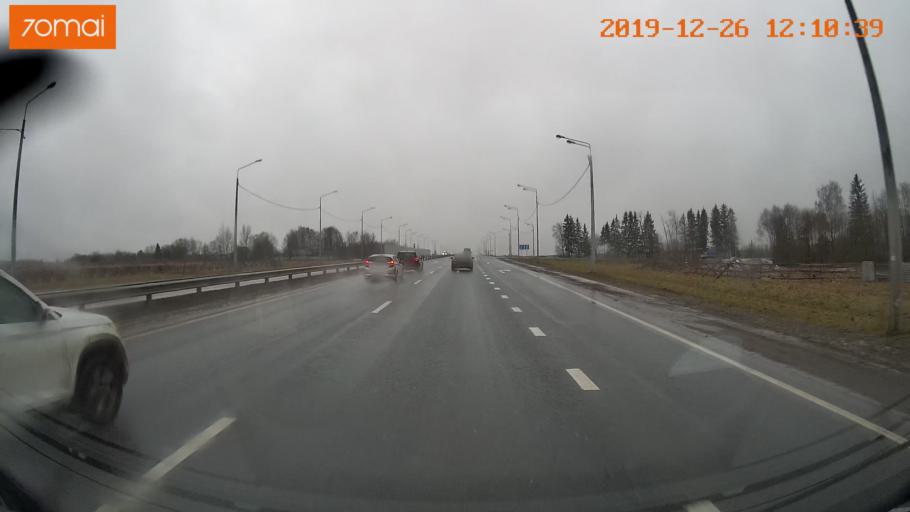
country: RU
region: Vologda
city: Tonshalovo
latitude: 59.2574
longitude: 37.9773
